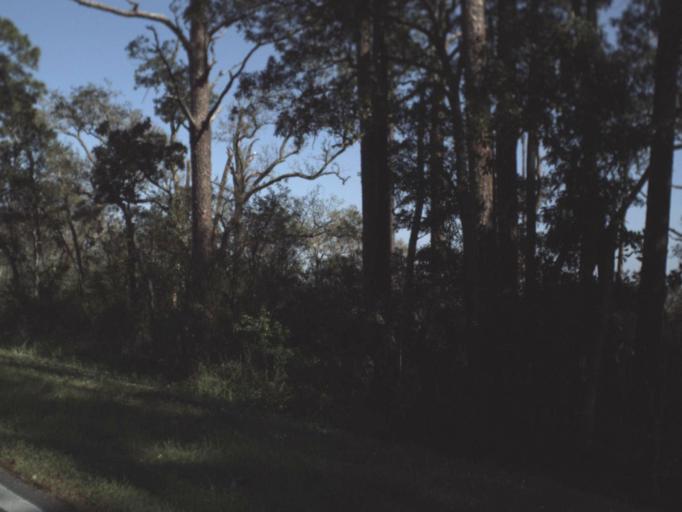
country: US
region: Florida
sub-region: Franklin County
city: Carrabelle
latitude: 29.8627
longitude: -84.6232
